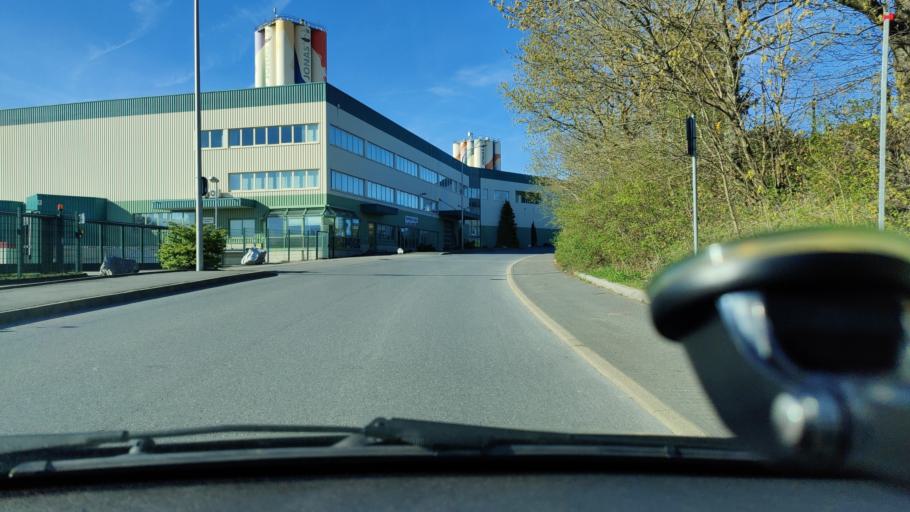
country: DE
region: North Rhine-Westphalia
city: Wulfrath
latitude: 51.2942
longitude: 7.0523
